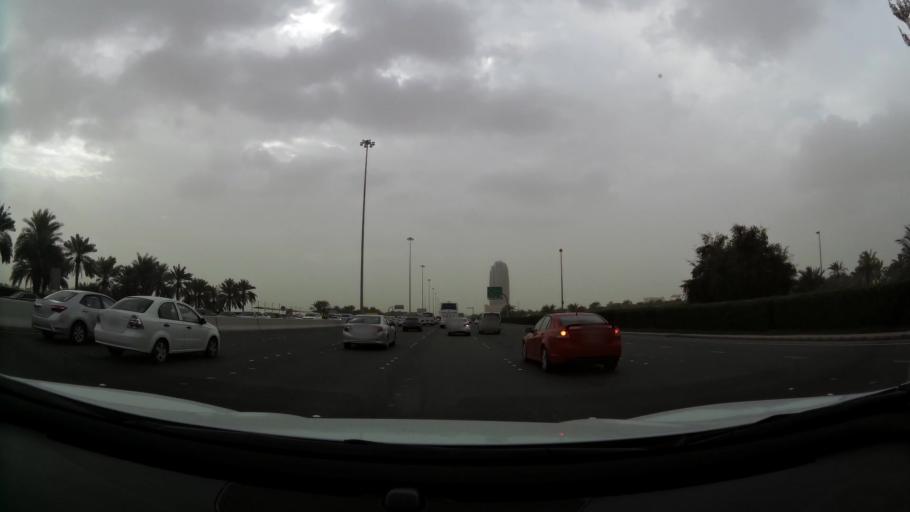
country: AE
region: Abu Dhabi
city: Abu Dhabi
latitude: 24.4659
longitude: 54.3970
